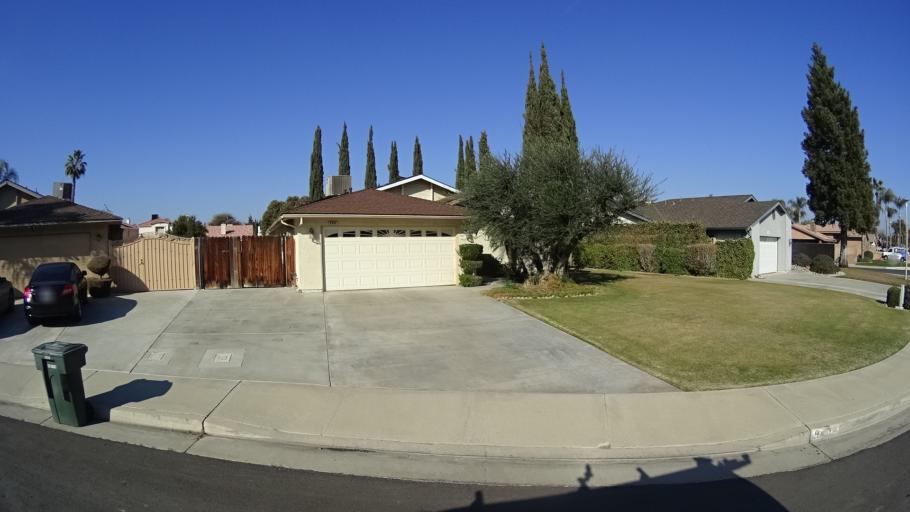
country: US
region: California
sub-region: Kern County
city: Greenacres
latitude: 35.3175
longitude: -119.1072
